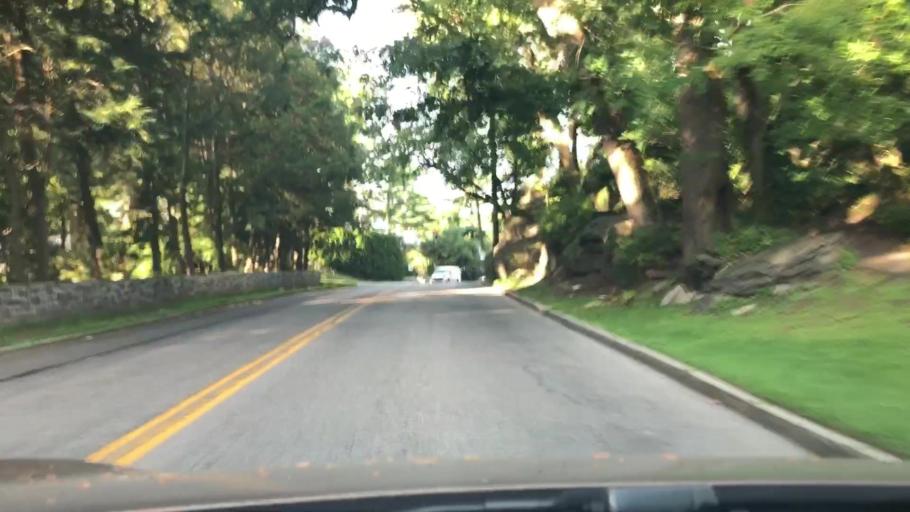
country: US
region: New York
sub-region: Westchester County
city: Bronxville
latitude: 40.9348
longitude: -73.8246
